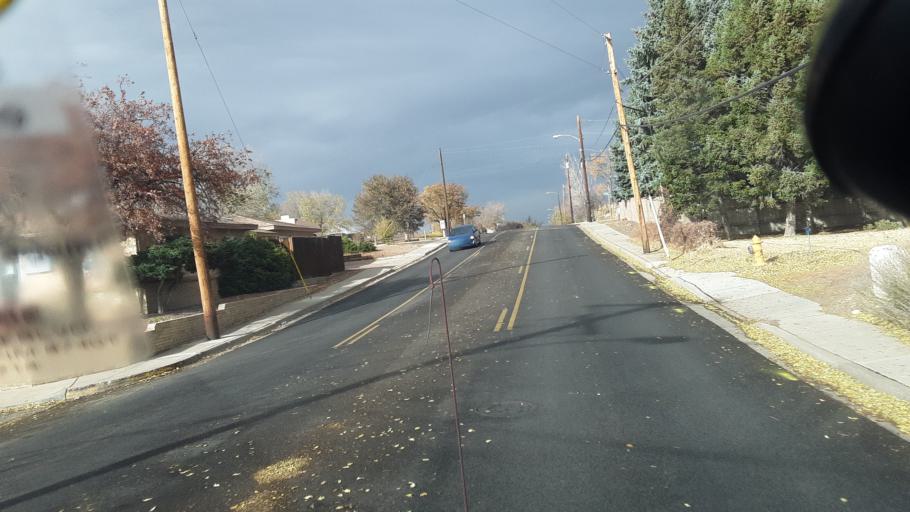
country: US
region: New Mexico
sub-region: San Juan County
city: Farmington
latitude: 36.7346
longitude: -108.1980
